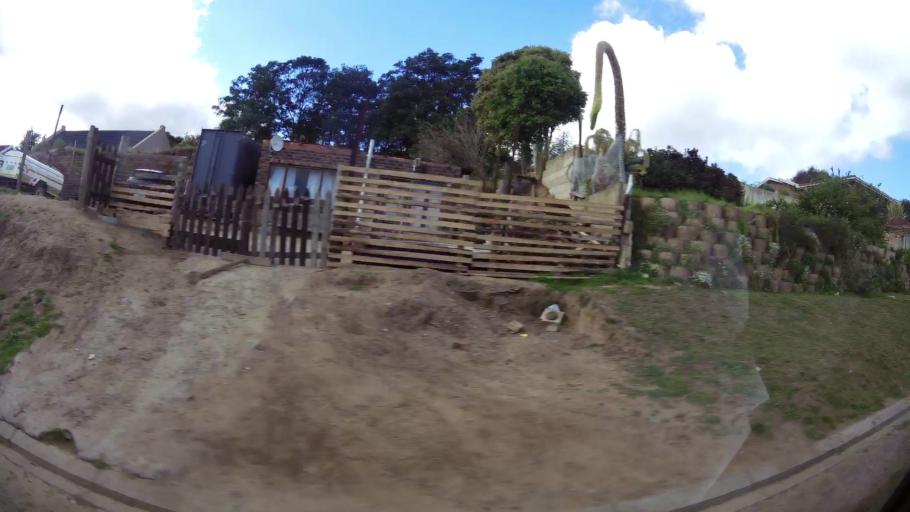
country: ZA
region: Western Cape
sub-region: Eden District Municipality
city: Knysna
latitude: -34.0462
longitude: 23.0868
